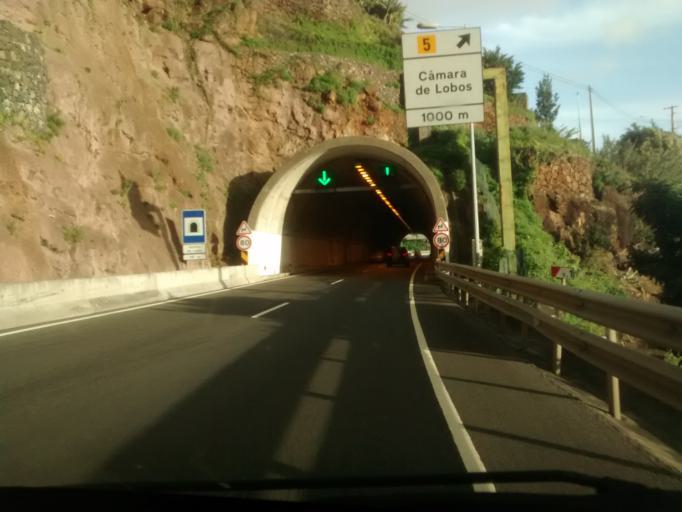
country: PT
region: Madeira
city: Camara de Lobos
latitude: 32.6617
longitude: -16.9798
